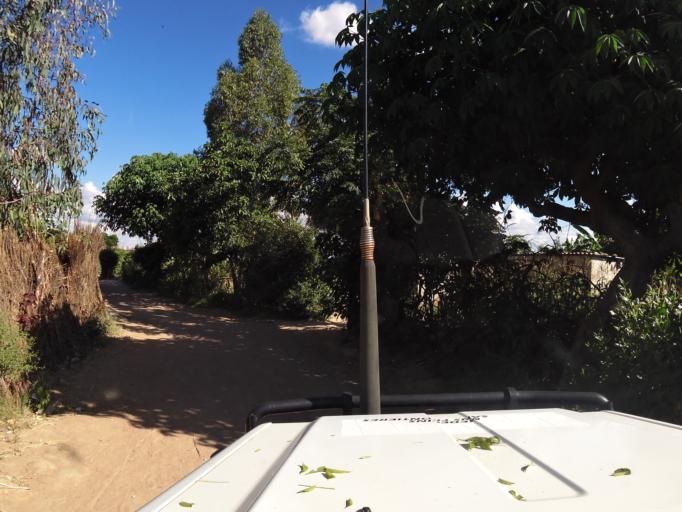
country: ZW
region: Harare
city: Epworth
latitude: -17.8775
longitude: 31.1357
